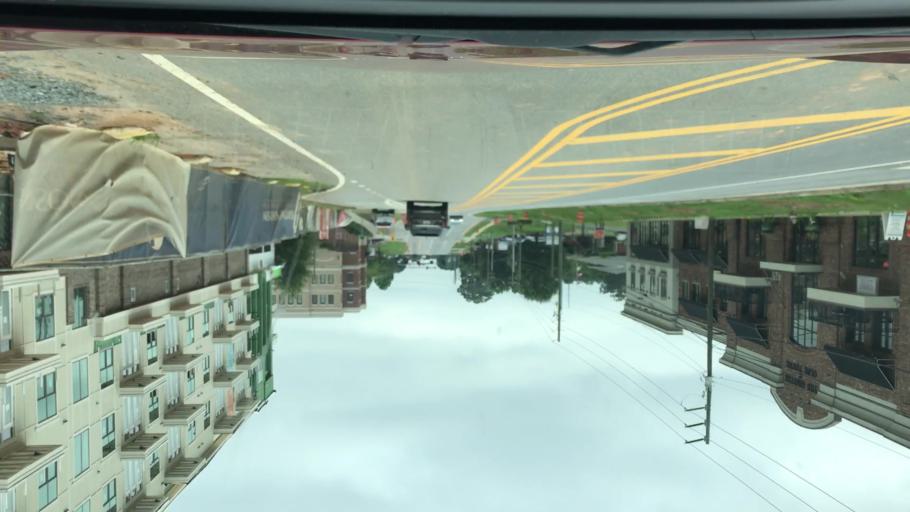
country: US
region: Georgia
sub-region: Gwinnett County
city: Suwanee
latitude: 34.0546
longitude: -84.0677
